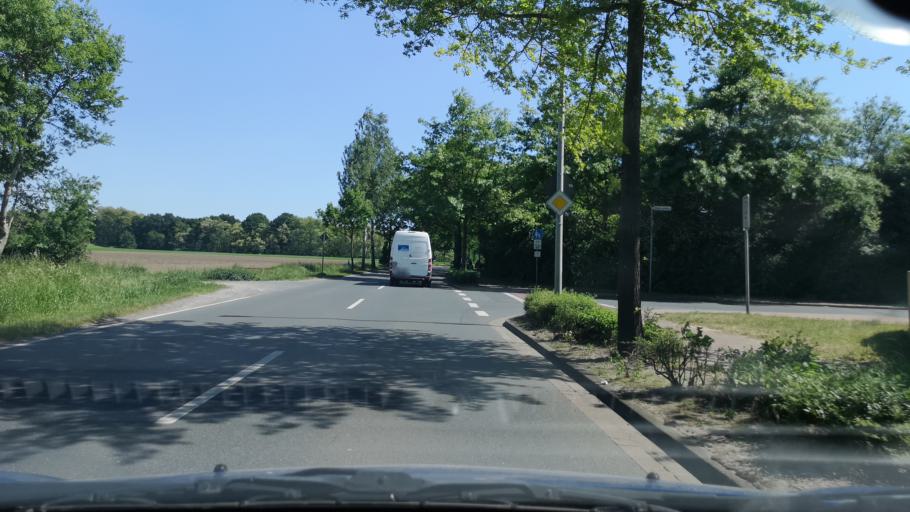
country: DE
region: Lower Saxony
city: Garbsen-Mitte
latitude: 52.4434
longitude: 9.6172
